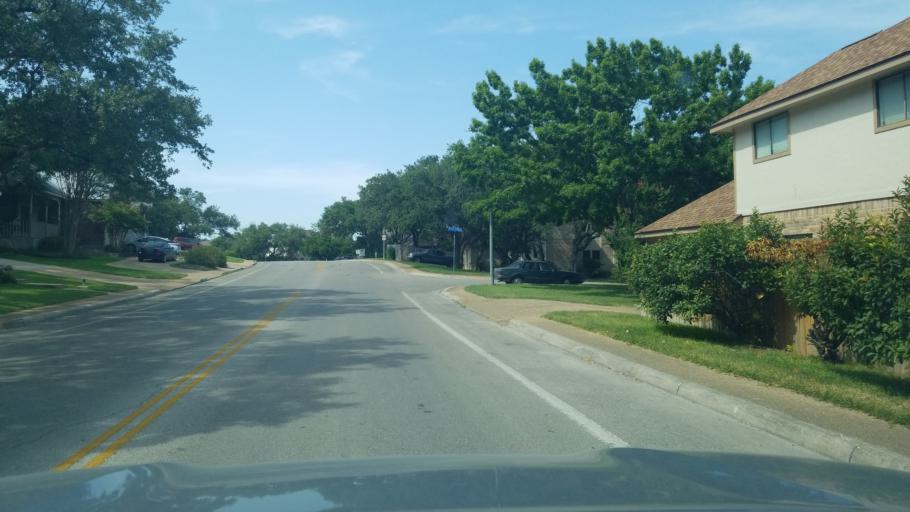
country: US
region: Texas
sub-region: Bexar County
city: Hollywood Park
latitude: 29.6282
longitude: -98.4877
